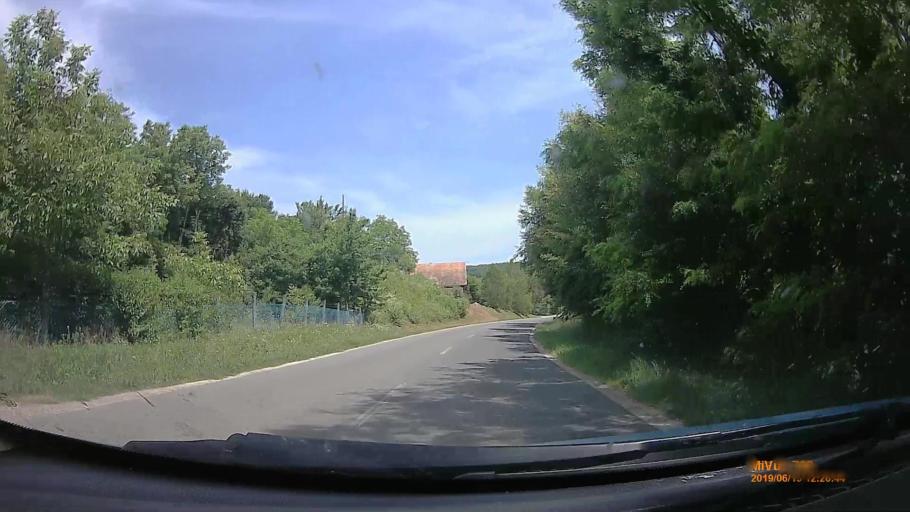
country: HU
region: Baranya
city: Buekkoesd
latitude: 46.1237
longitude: 18.0017
